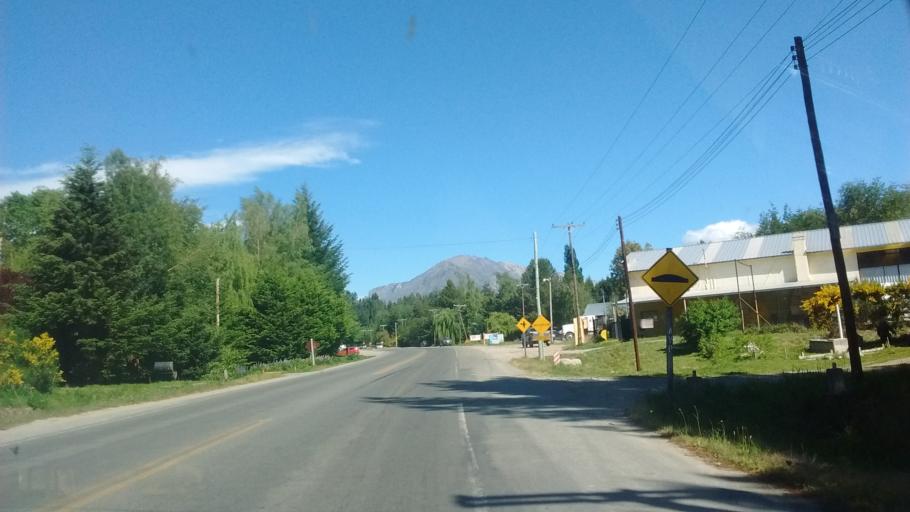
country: AR
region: Chubut
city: Lago Puelo
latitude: -42.0320
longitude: -71.5670
